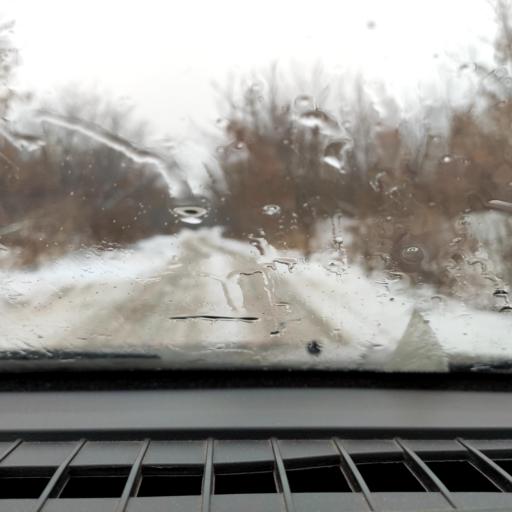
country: RU
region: Samara
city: Tol'yatti
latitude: 53.5627
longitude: 49.3273
